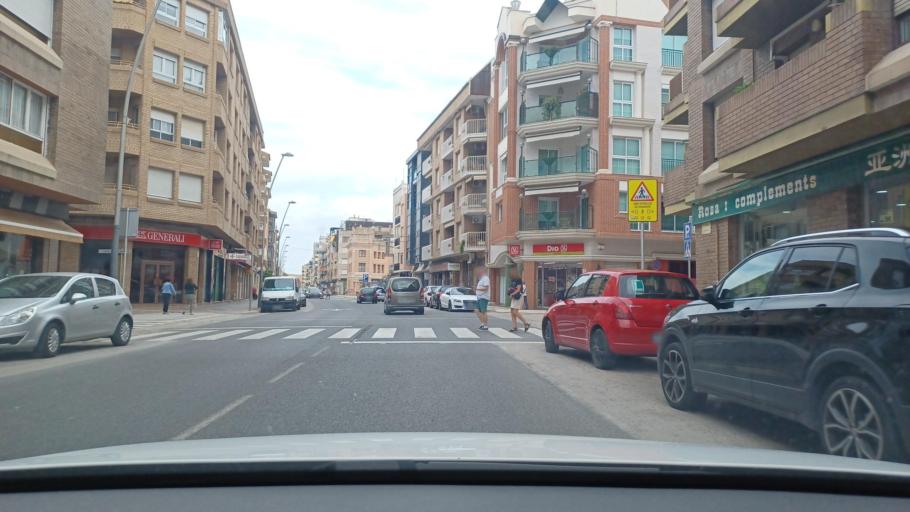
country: ES
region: Catalonia
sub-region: Provincia de Tarragona
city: Tortosa
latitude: 40.8044
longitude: 0.5205
